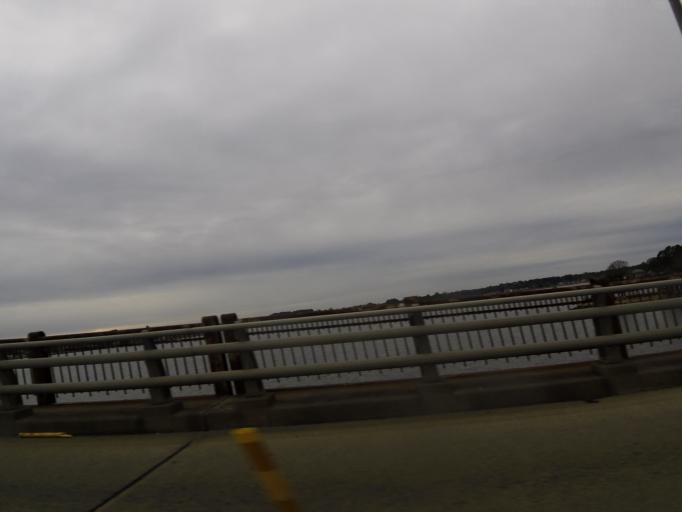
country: US
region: Virginia
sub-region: City of Portsmouth
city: Portsmouth Heights
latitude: 36.8433
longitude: -76.3638
